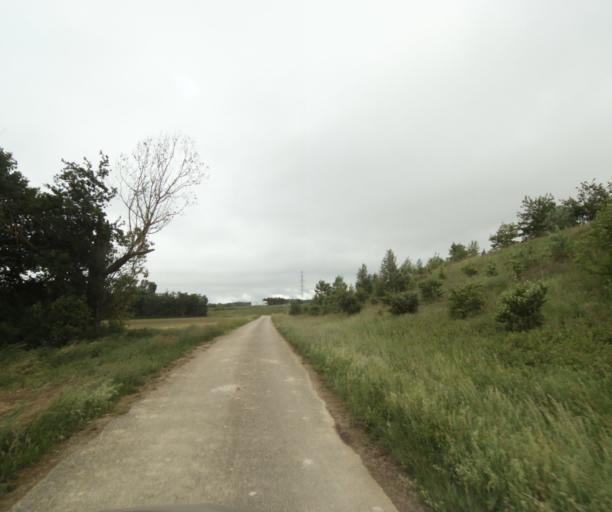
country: FR
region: Rhone-Alpes
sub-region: Departement de l'Ain
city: Tramoyes
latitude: 45.8602
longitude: 4.9482
